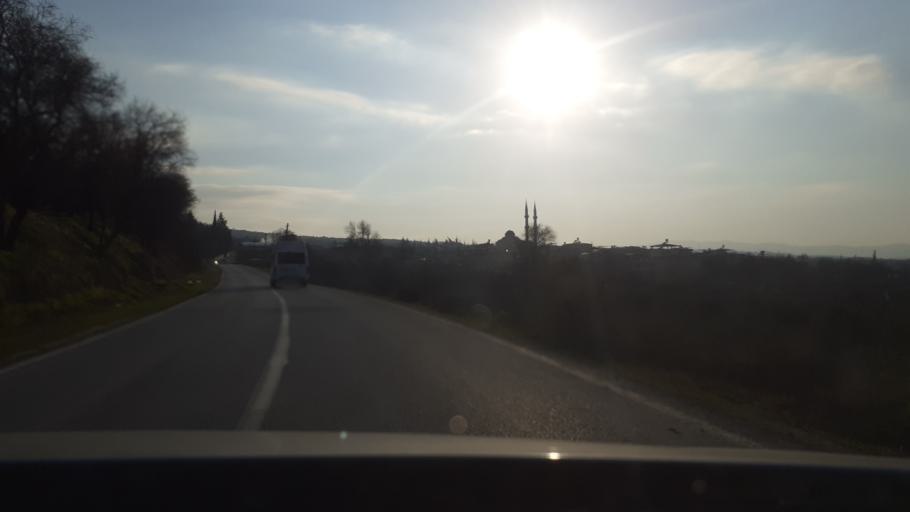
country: TR
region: Hatay
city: Oymakli
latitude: 36.1152
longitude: 36.3023
